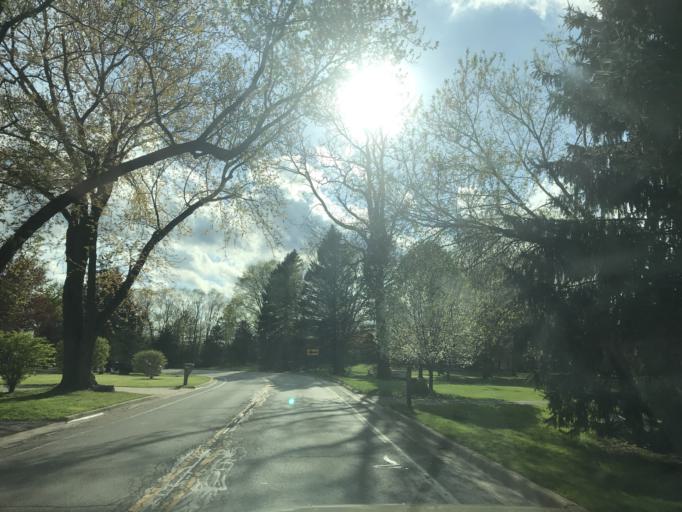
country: US
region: Michigan
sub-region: Livingston County
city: Brighton
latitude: 42.5452
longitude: -83.7470
